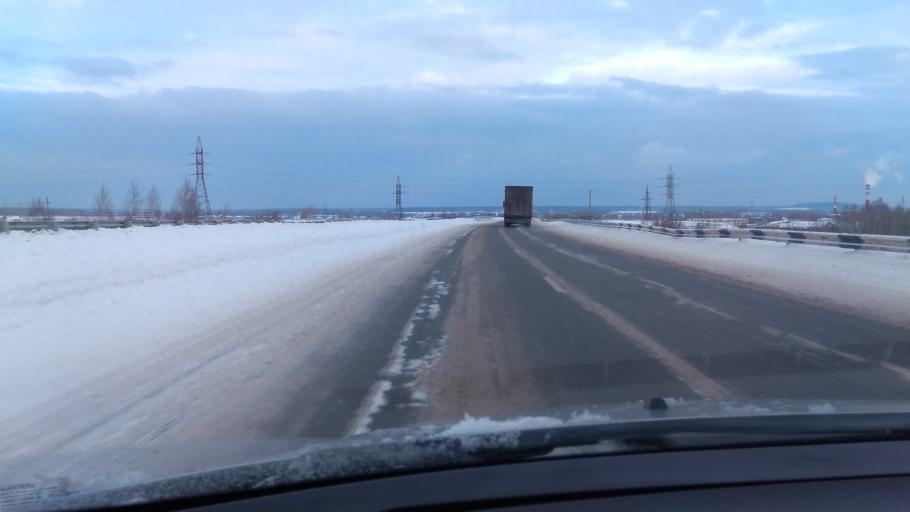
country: RU
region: Sverdlovsk
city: Tsementnyy
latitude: 57.4766
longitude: 60.1805
